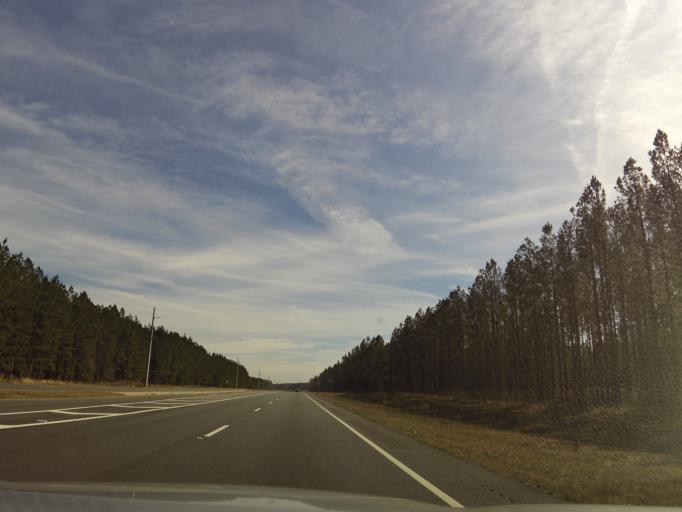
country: US
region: Georgia
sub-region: Glynn County
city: Dock Junction
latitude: 31.2278
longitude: -81.7387
